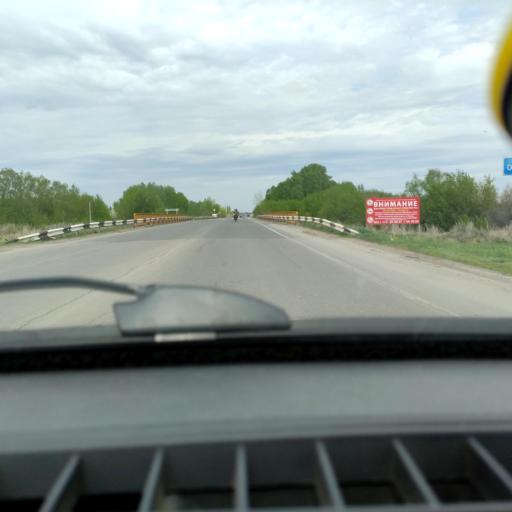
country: RU
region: Samara
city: Tol'yatti
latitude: 53.6941
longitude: 49.4190
